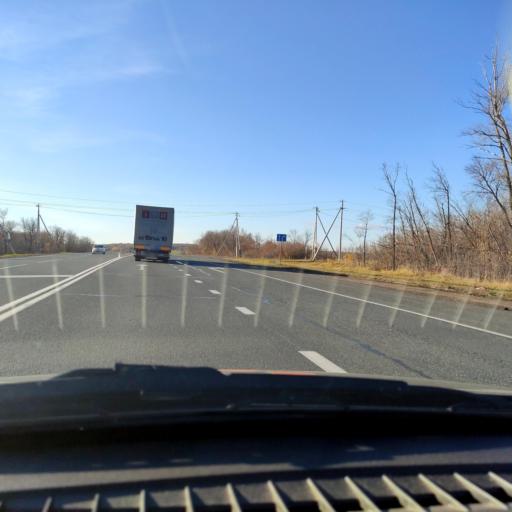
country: RU
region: Samara
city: Mezhdurechensk
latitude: 53.2562
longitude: 49.1304
